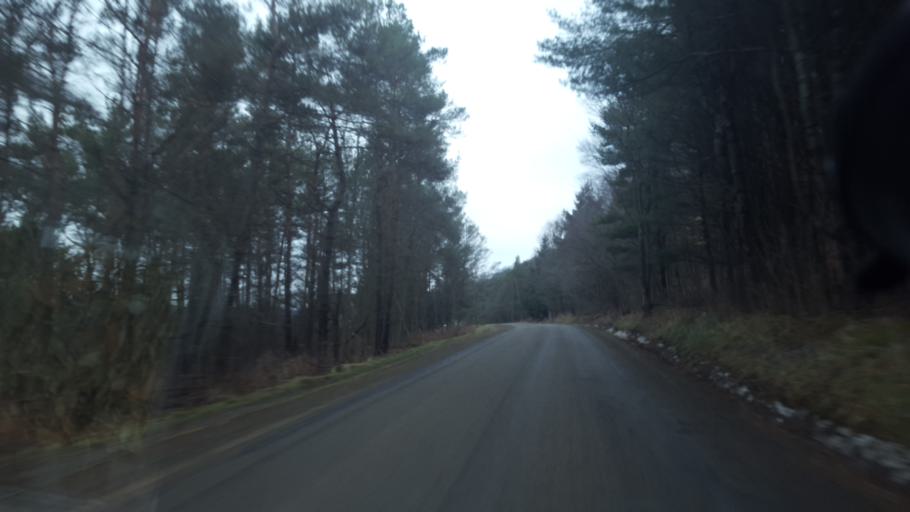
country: US
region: New York
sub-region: Allegany County
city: Wellsville
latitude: 41.9650
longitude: -77.8473
